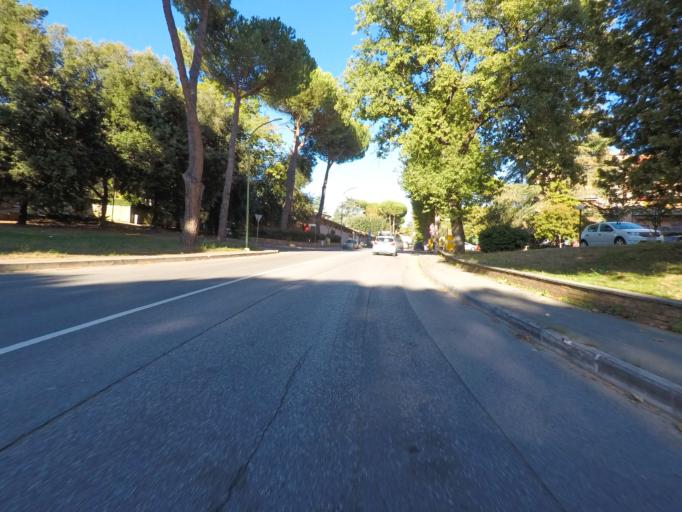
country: IT
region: Tuscany
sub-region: Provincia di Siena
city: Belverde
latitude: 43.3395
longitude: 11.3008
